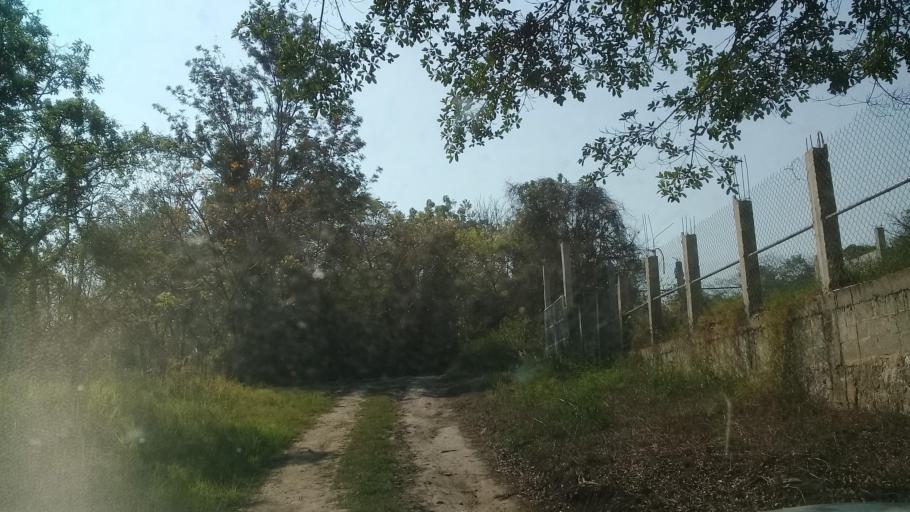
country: MX
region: Veracruz
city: El Castillo
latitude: 19.5724
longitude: -96.8366
